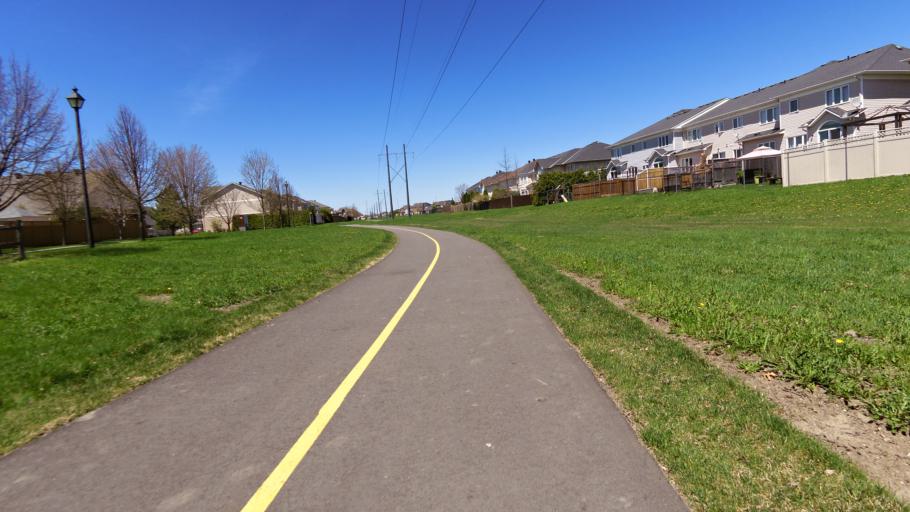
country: CA
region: Ontario
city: Clarence-Rockland
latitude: 45.4546
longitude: -75.4704
